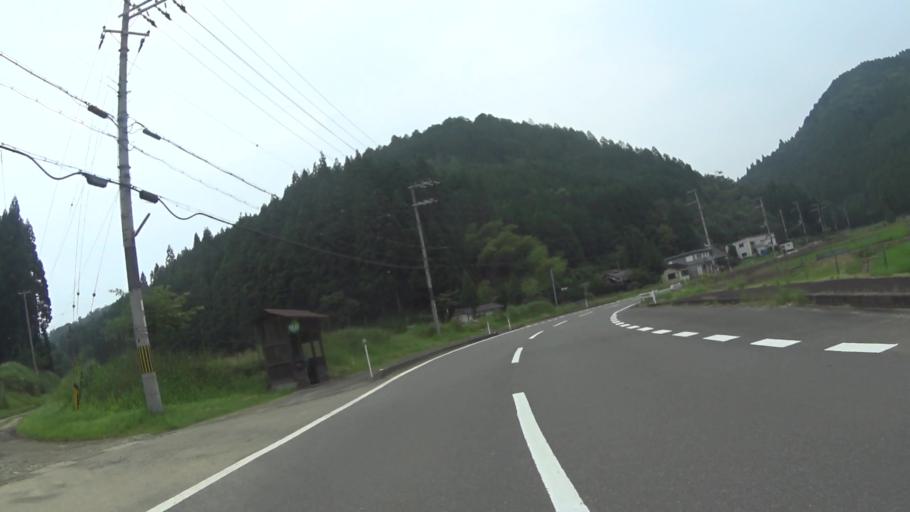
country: JP
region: Kyoto
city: Kameoka
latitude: 35.1599
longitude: 135.6007
